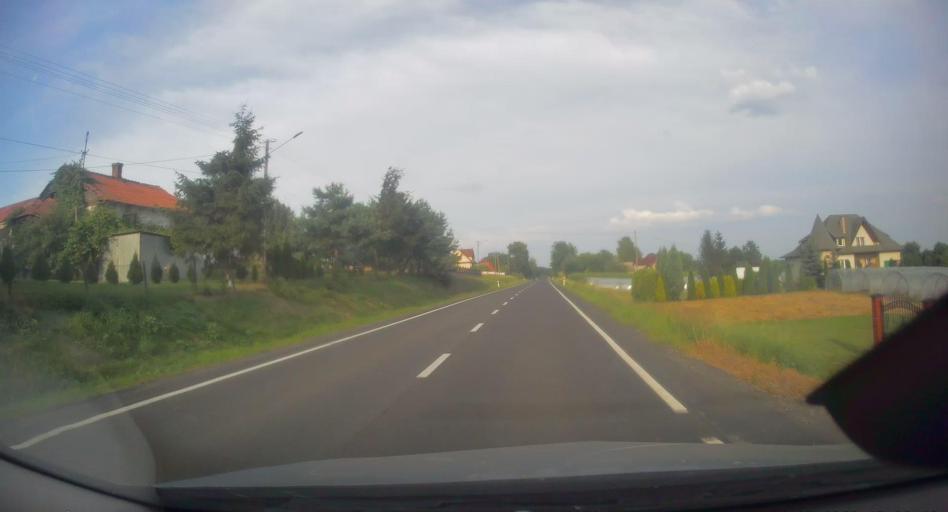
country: PL
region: Lesser Poland Voivodeship
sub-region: Powiat bochenski
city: Dziewin
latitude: 50.1440
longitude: 20.4989
